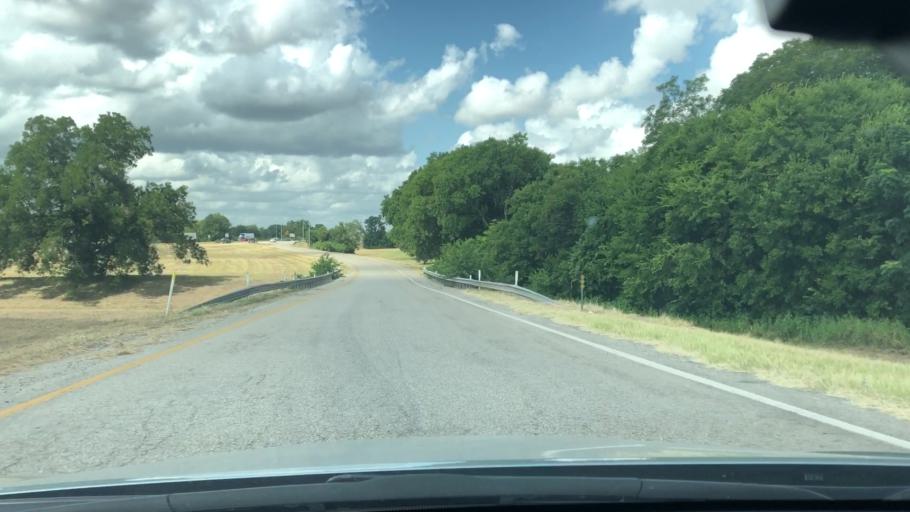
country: US
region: Texas
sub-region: Guadalupe County
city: McQueeney
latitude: 29.5718
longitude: -98.0168
